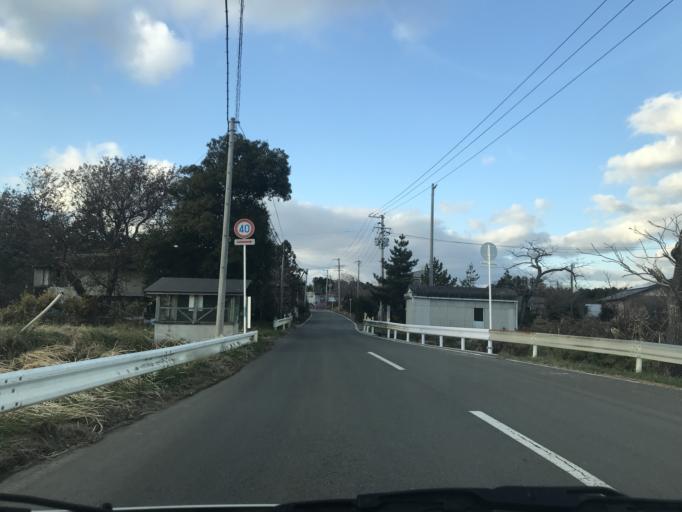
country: JP
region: Miyagi
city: Kogota
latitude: 38.6387
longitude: 141.0525
